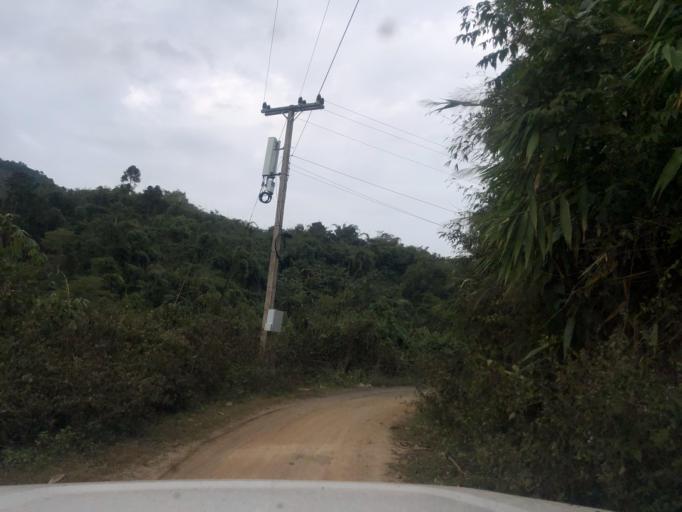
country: LA
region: Phongsali
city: Khoa
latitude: 21.3001
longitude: 102.5838
